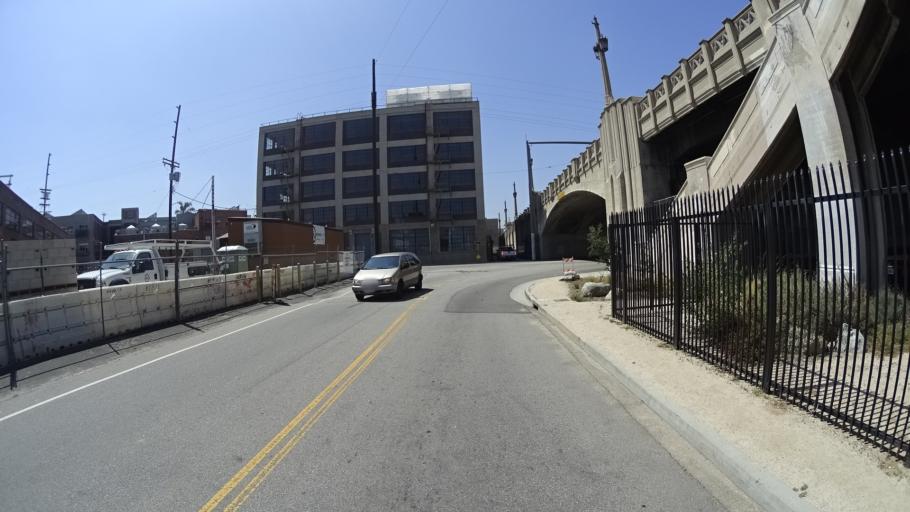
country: US
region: California
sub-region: Los Angeles County
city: Los Angeles
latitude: 34.0417
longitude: -118.2323
